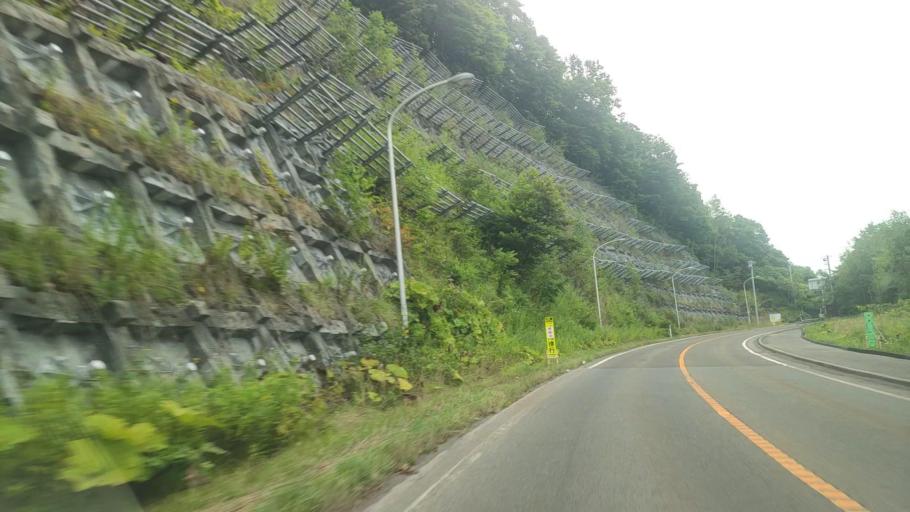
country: JP
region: Hokkaido
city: Otaru
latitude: 43.1352
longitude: 141.0390
